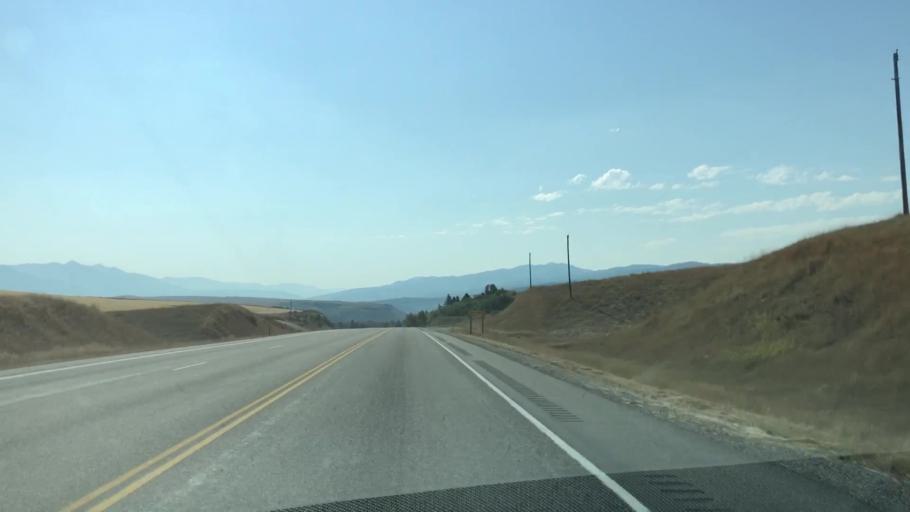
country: US
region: Idaho
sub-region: Teton County
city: Victor
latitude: 43.4942
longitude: -111.4571
